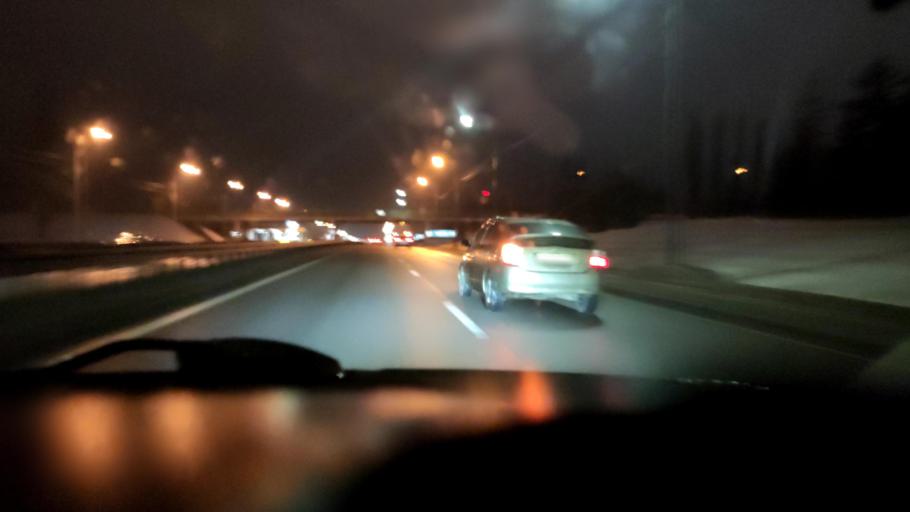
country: RU
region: Voronezj
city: Ramon'
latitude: 51.9318
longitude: 39.2209
